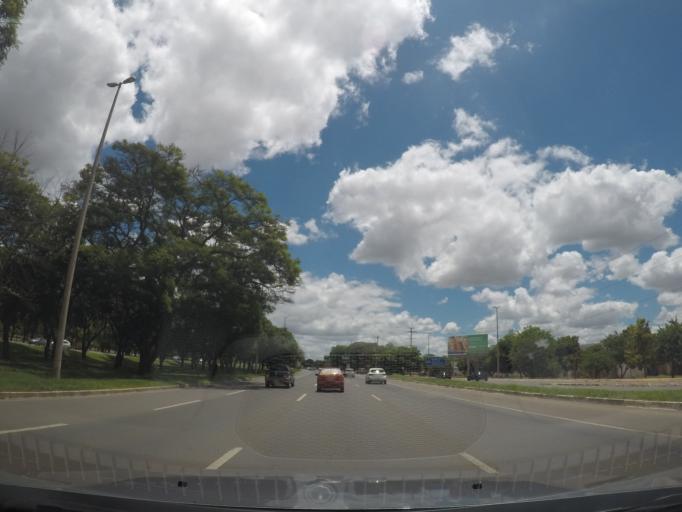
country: BR
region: Federal District
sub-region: Brasilia
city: Brasilia
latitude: -15.8034
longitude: -47.9475
